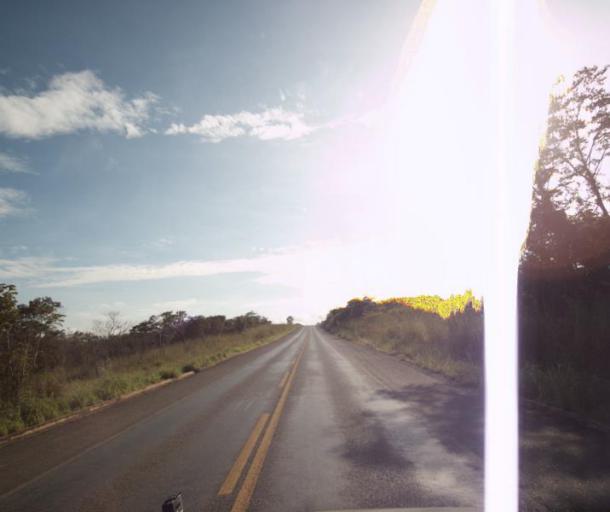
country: BR
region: Goias
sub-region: Pirenopolis
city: Pirenopolis
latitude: -15.5810
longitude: -48.6287
